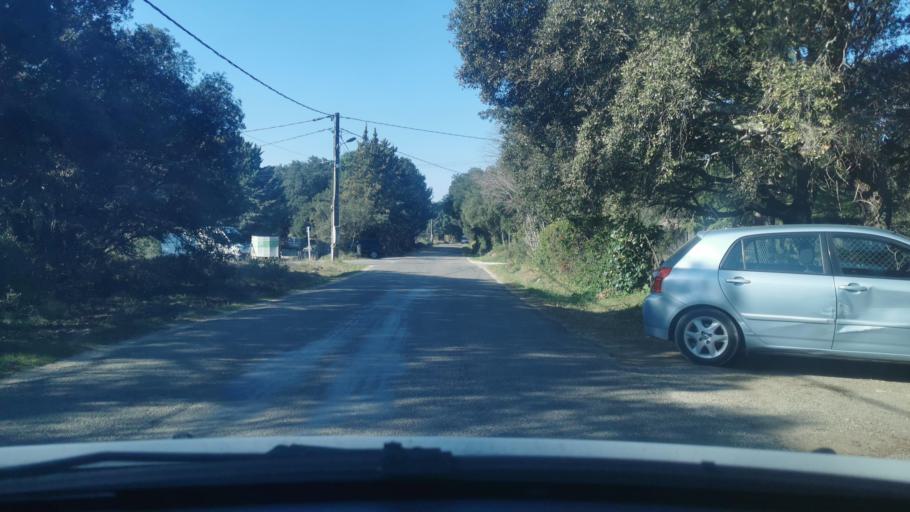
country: FR
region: Languedoc-Roussillon
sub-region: Departement du Gard
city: Montaren-et-Saint-Mediers
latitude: 44.0451
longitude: 4.3927
